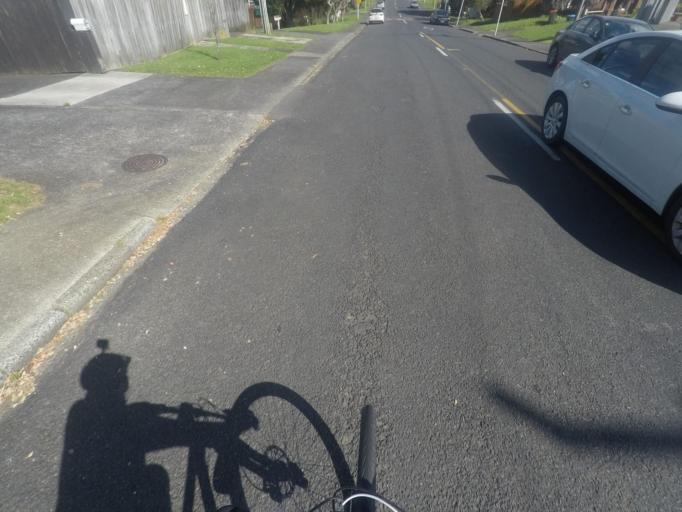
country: NZ
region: Auckland
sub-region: Auckland
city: Auckland
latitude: -36.9209
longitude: 174.7585
